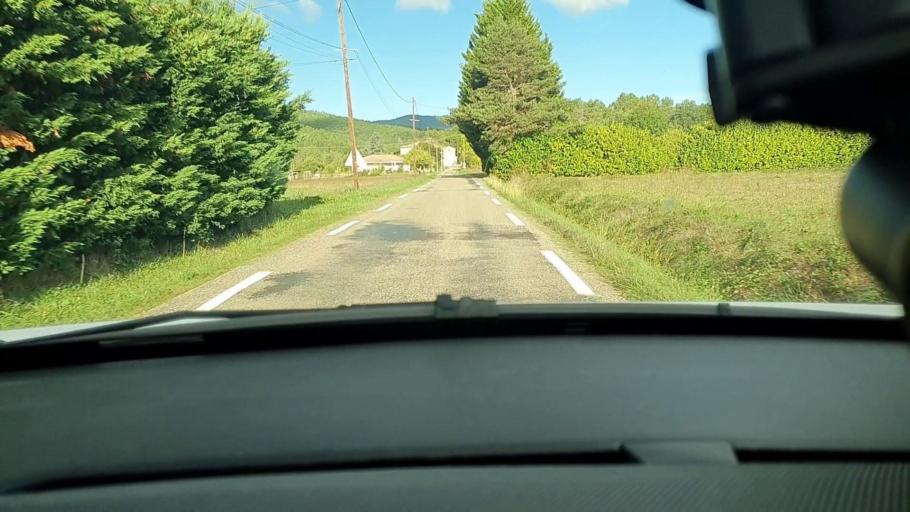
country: FR
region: Languedoc-Roussillon
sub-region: Departement du Gard
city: Besseges
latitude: 44.3203
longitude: 4.1270
